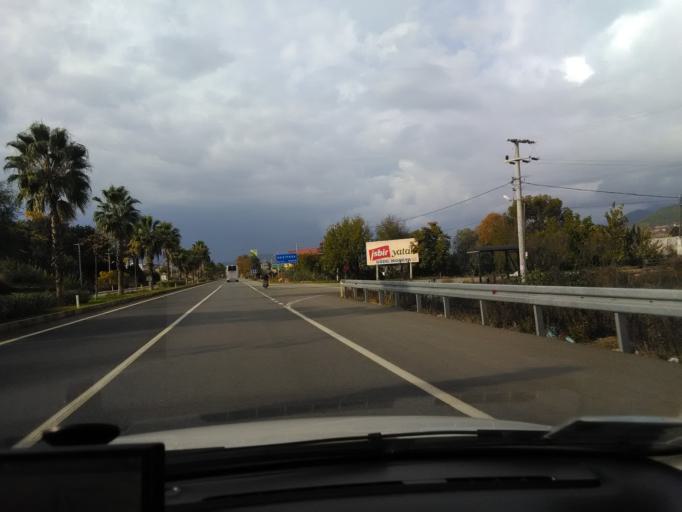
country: TR
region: Antalya
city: Gazipasa
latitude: 36.2499
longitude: 32.3402
